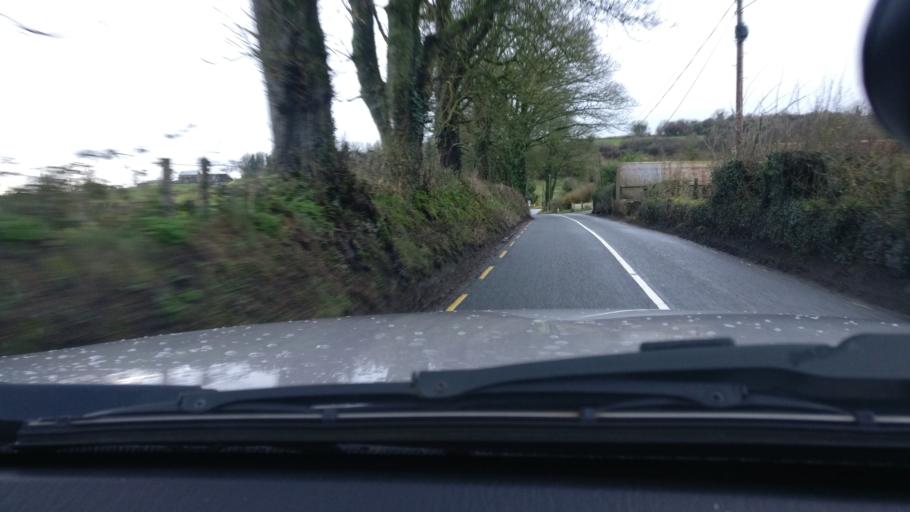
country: IE
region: Leinster
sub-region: An Longfort
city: Granard
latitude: 53.8054
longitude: -7.3784
